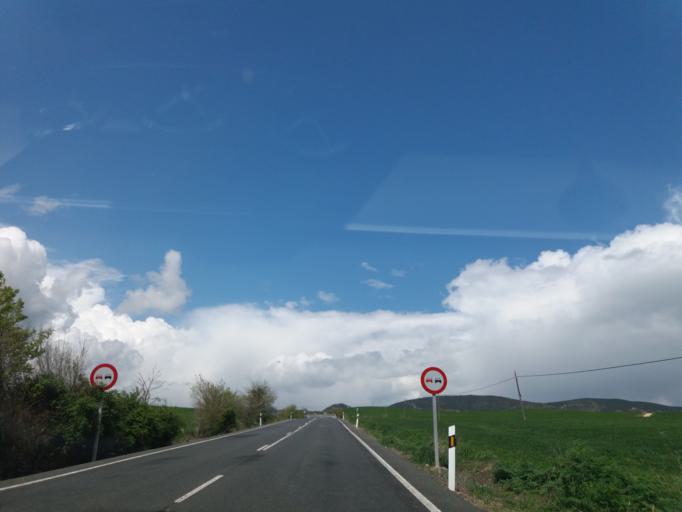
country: ES
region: La Rioja
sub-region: Provincia de La Rioja
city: Fonzaleche
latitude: 42.5894
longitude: -3.0340
